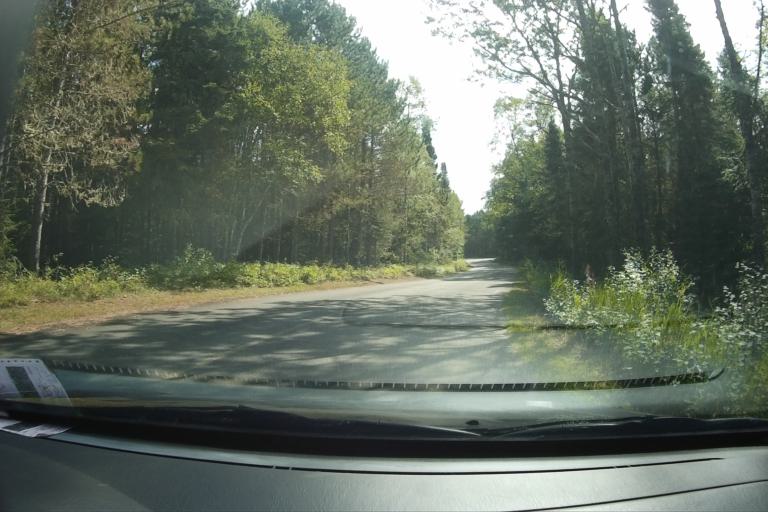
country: CA
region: Ontario
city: Marathon
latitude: 48.7895
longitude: -86.6252
